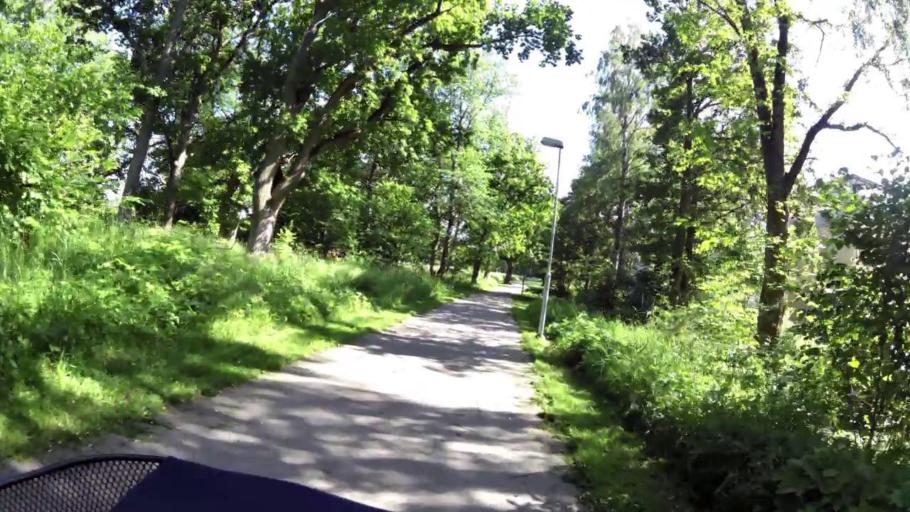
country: SE
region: OEstergoetland
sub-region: Linkopings Kommun
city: Linkoping
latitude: 58.3841
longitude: 15.6400
